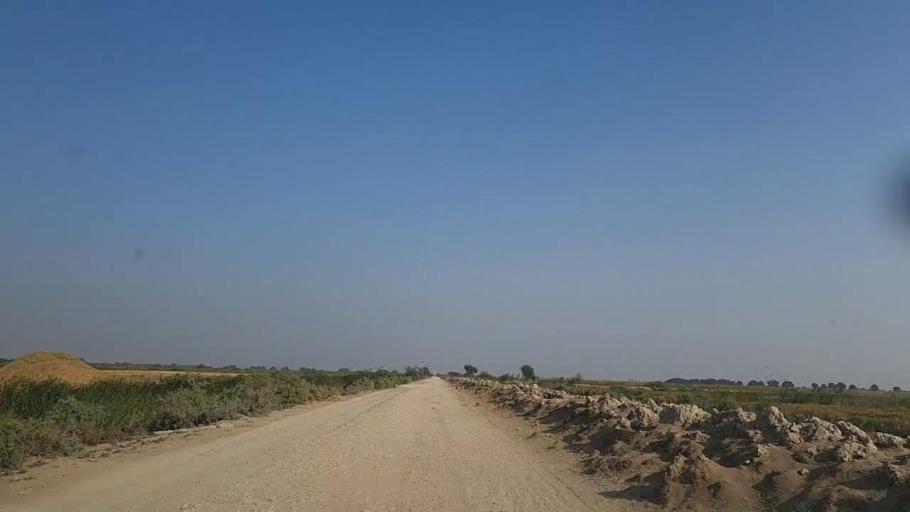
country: PK
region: Sindh
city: Jati
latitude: 24.4604
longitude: 68.2945
